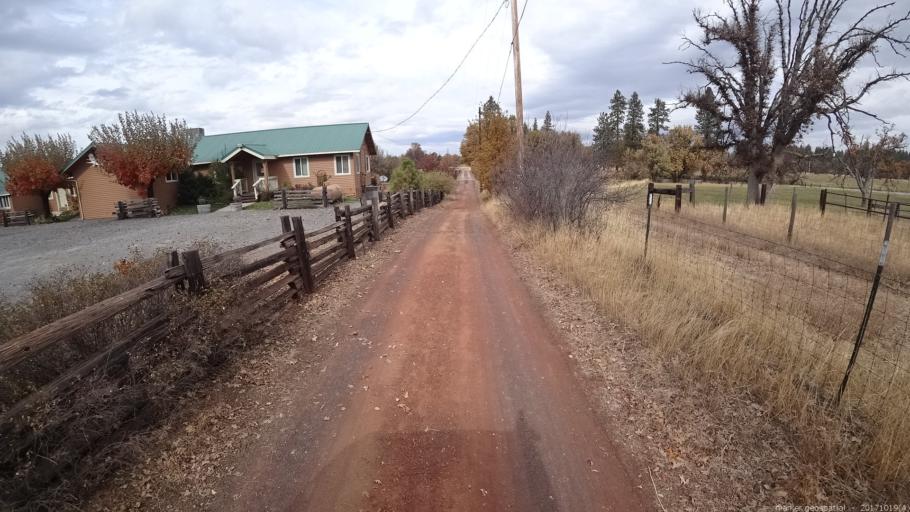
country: US
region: California
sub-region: Shasta County
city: Burney
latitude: 41.0965
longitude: -121.5482
